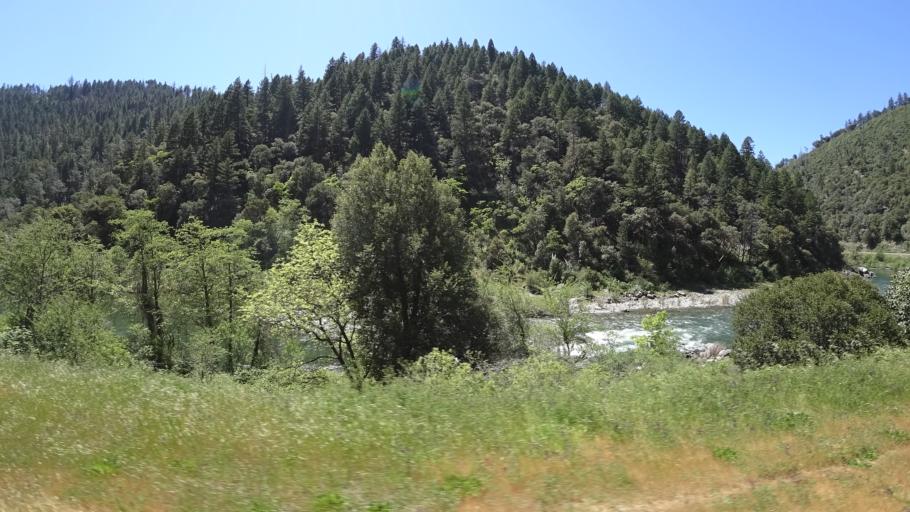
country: US
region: California
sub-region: Trinity County
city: Hayfork
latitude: 40.7661
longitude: -123.2924
